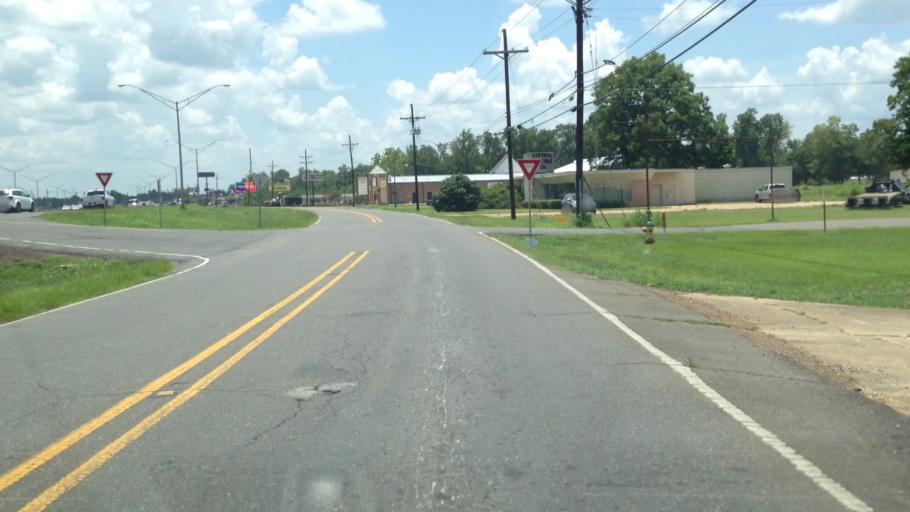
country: US
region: Louisiana
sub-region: Rapides Parish
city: Alexandria
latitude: 31.3091
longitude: -92.4793
